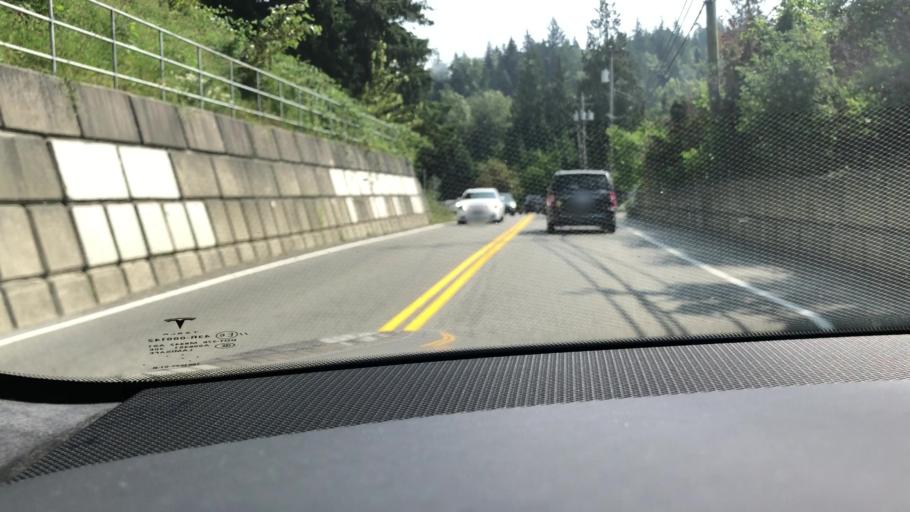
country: CA
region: British Columbia
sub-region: Fraser Valley Regional District
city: Chilliwack
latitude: 49.0940
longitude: -121.9721
